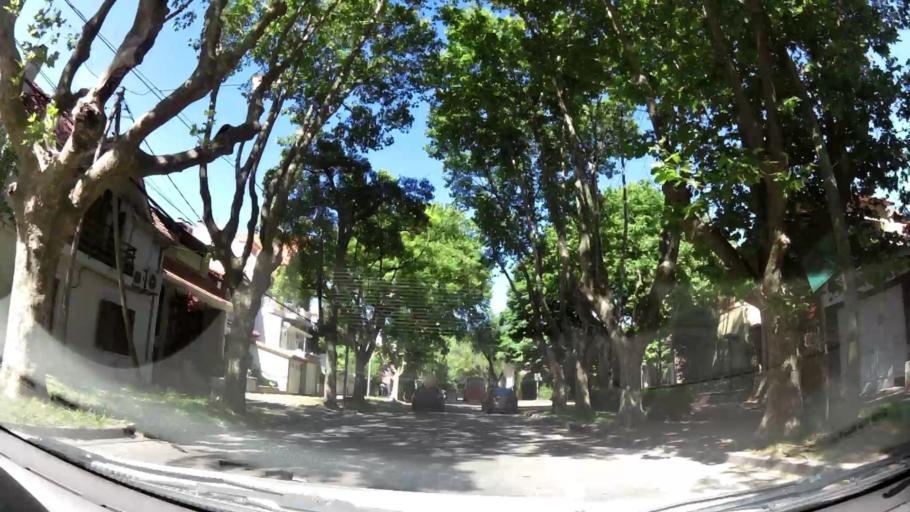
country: AR
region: Buenos Aires
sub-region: Partido de Vicente Lopez
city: Olivos
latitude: -34.5186
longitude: -58.4807
